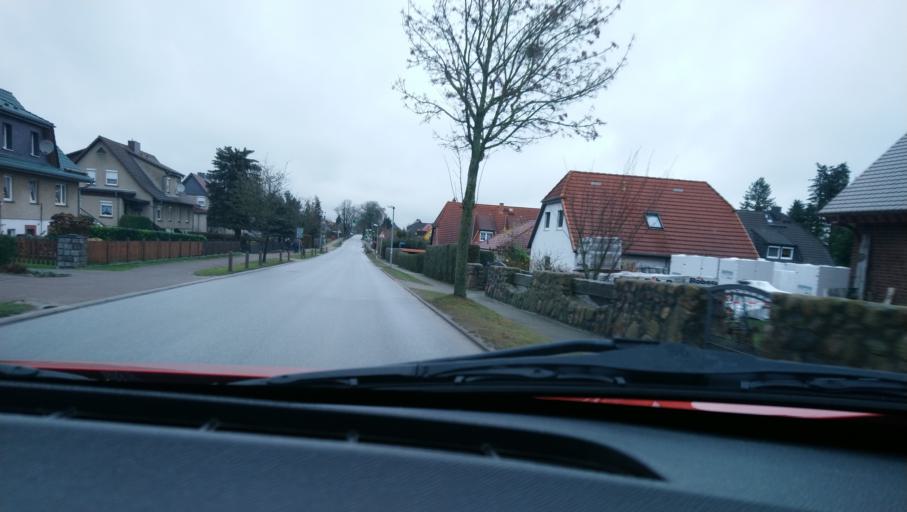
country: DE
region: Mecklenburg-Vorpommern
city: Seehof
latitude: 53.6916
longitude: 11.4310
